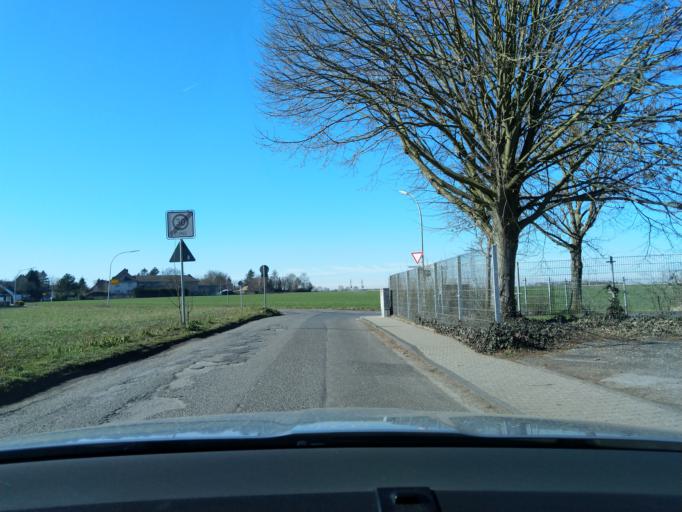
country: DE
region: North Rhine-Westphalia
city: Erkelenz
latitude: 51.1069
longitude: 6.3773
